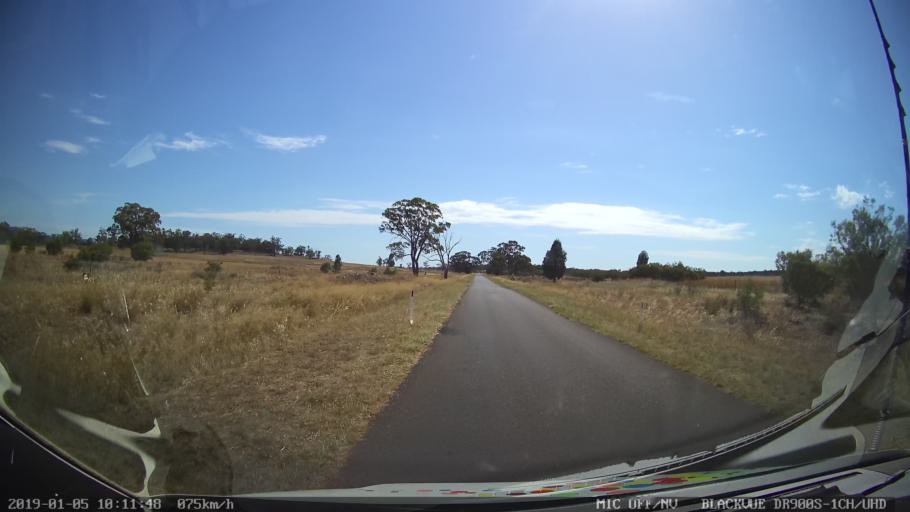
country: AU
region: New South Wales
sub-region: Gilgandra
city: Gilgandra
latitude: -31.6113
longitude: 148.9055
